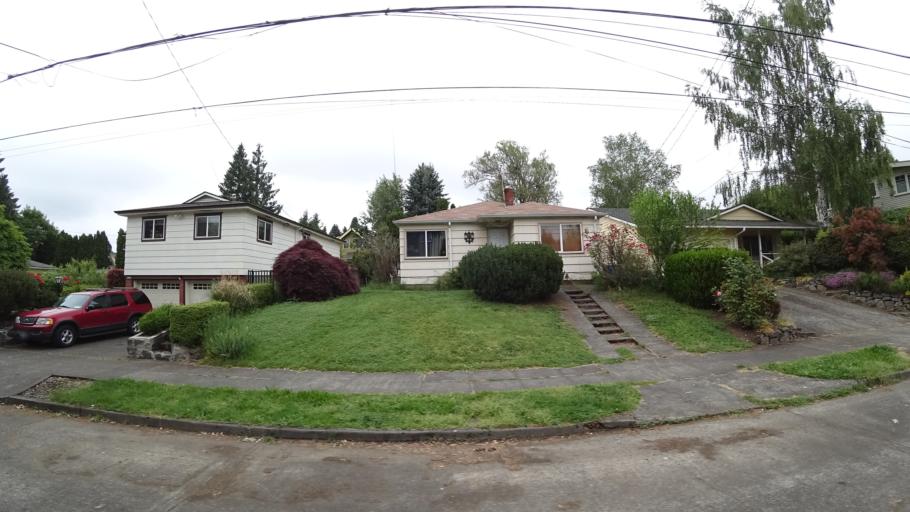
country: US
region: Oregon
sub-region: Multnomah County
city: Lents
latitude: 45.5027
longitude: -122.6188
